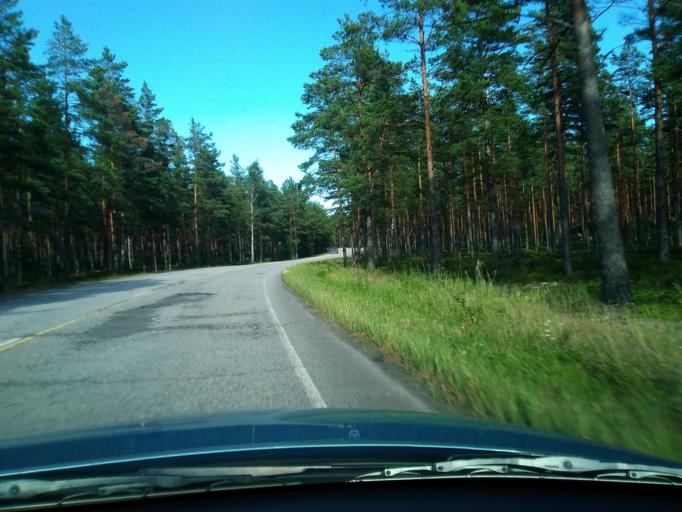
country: FI
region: Uusimaa
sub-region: Raaseporin
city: Ekenaes
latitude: 59.8987
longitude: 23.2259
